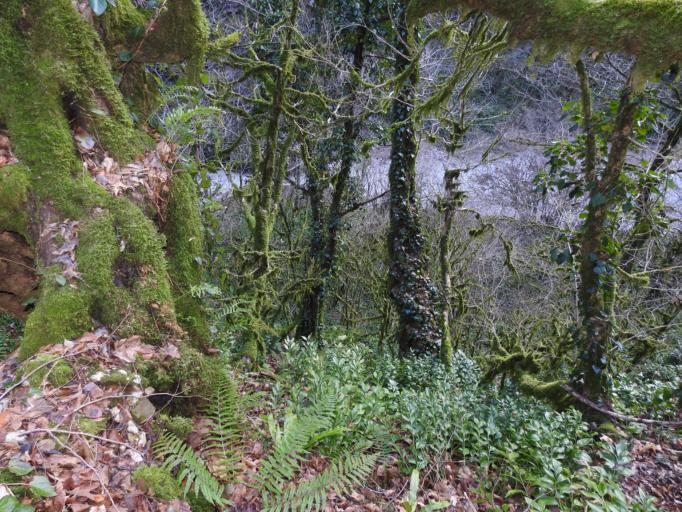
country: GE
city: Gantiadi
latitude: 43.4147
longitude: 40.2163
